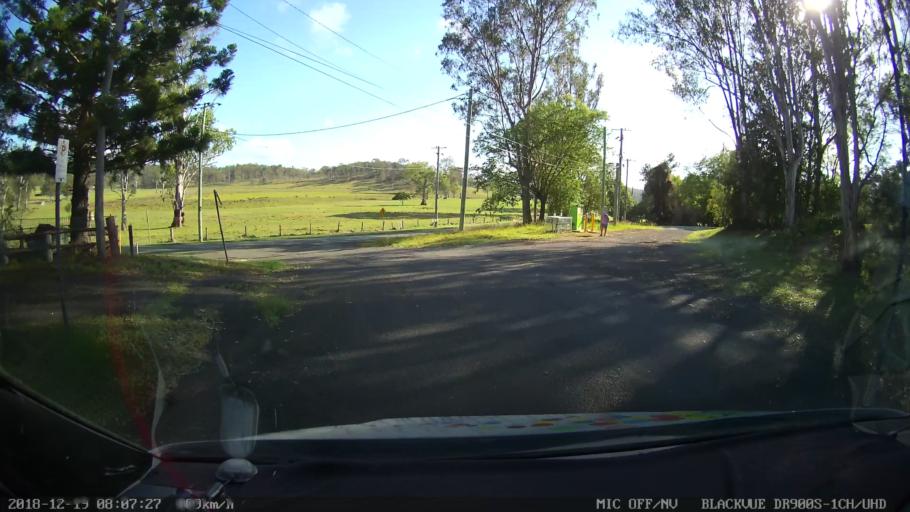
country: AU
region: Queensland
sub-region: Logan
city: Cedar Vale
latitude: -28.2117
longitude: 152.8650
